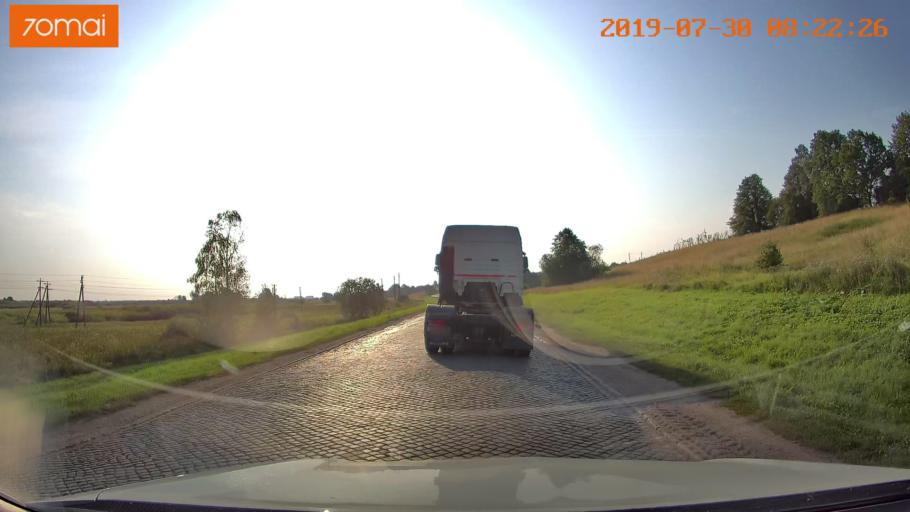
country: RU
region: Kaliningrad
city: Chernyakhovsk
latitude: 54.6255
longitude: 21.5339
